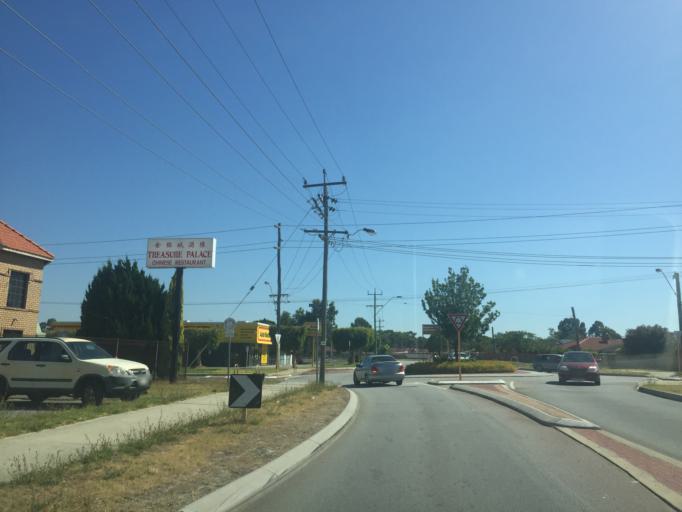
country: AU
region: Western Australia
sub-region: Gosnells
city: Maddington
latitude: -32.0499
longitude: 115.9766
